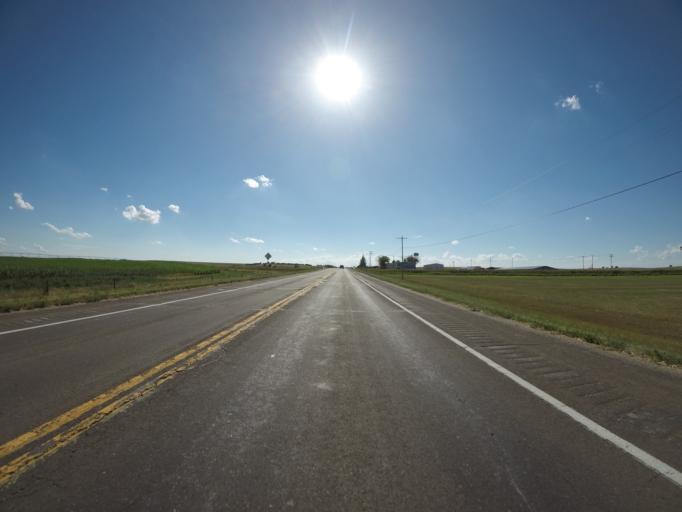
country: US
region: Colorado
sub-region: Logan County
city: Sterling
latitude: 40.6239
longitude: -103.3071
